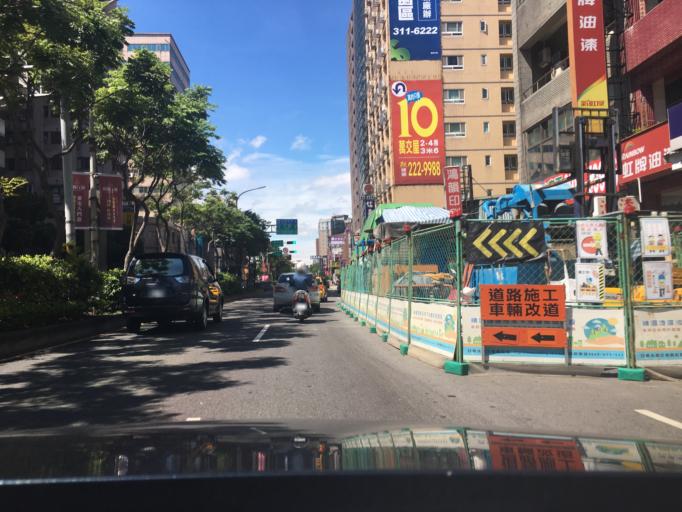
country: TW
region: Taiwan
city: Taoyuan City
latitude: 25.0511
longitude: 121.2893
